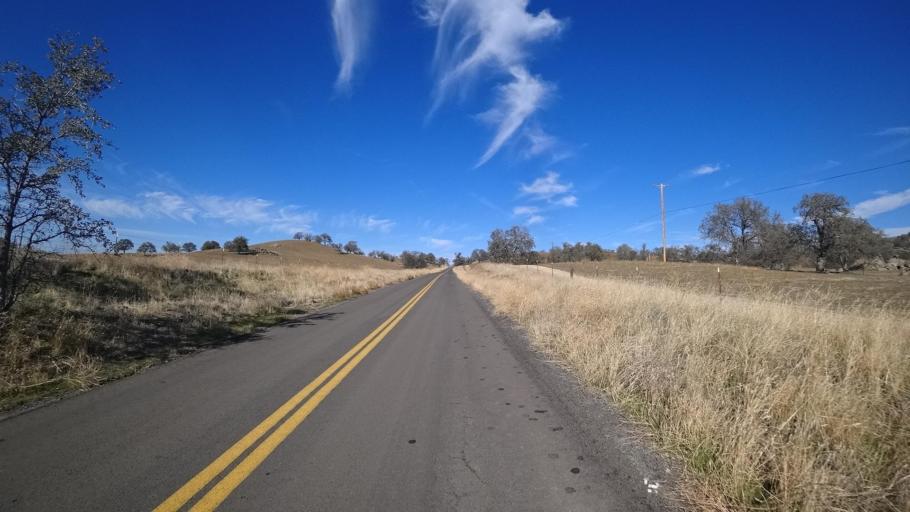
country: US
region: California
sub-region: Kern County
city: Oildale
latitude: 35.6413
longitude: -118.8376
